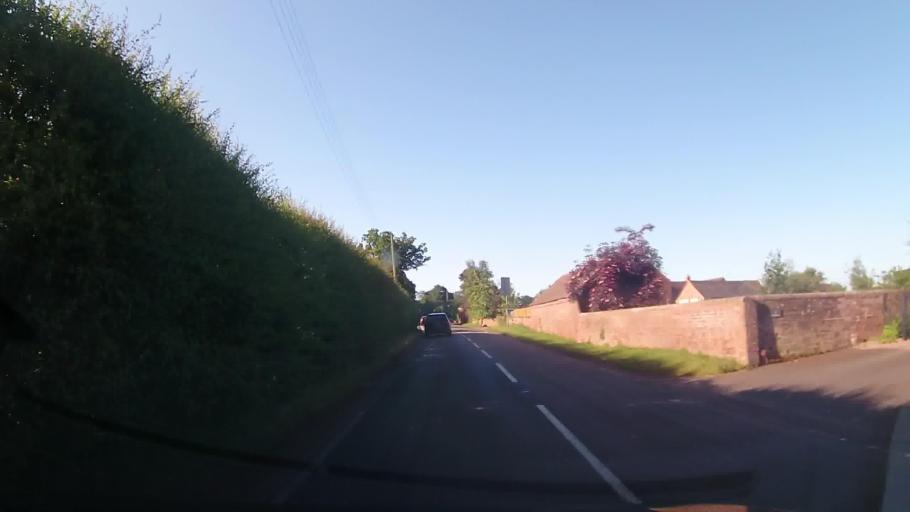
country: GB
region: England
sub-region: Shropshire
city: Withington
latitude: 52.7622
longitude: -2.6082
